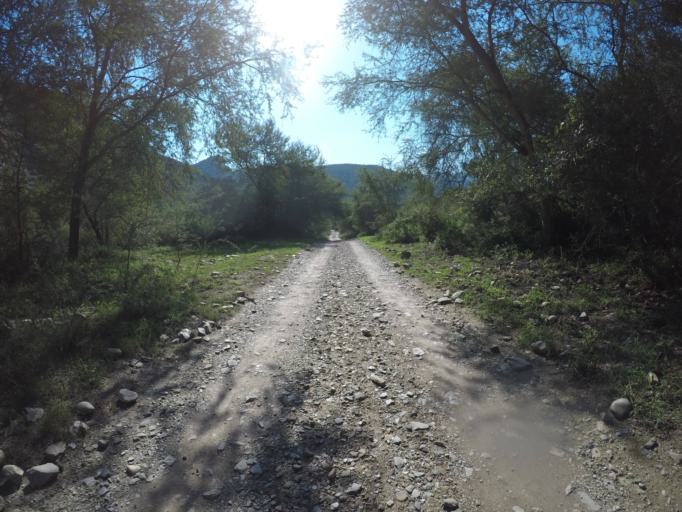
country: ZA
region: Eastern Cape
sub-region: Cacadu District Municipality
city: Kareedouw
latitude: -33.6579
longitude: 24.3661
